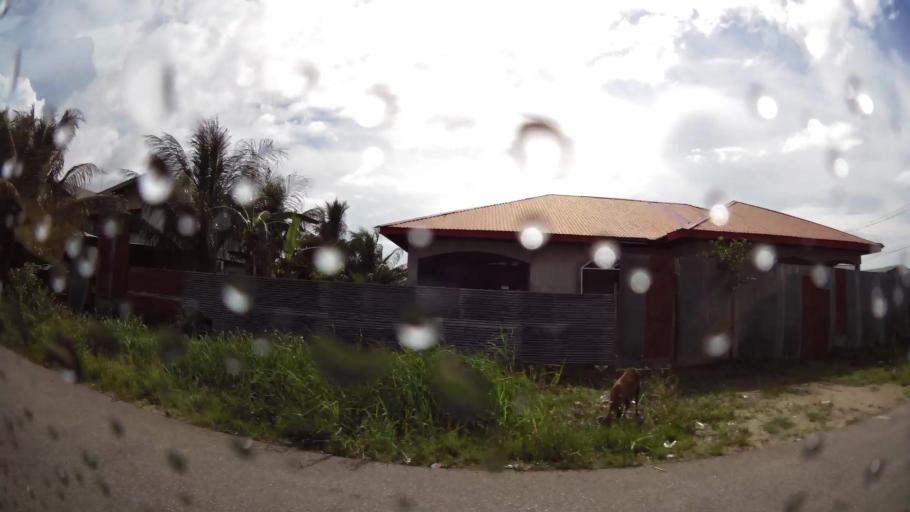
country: SR
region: Paramaribo
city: Paramaribo
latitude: 5.8452
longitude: -55.2048
